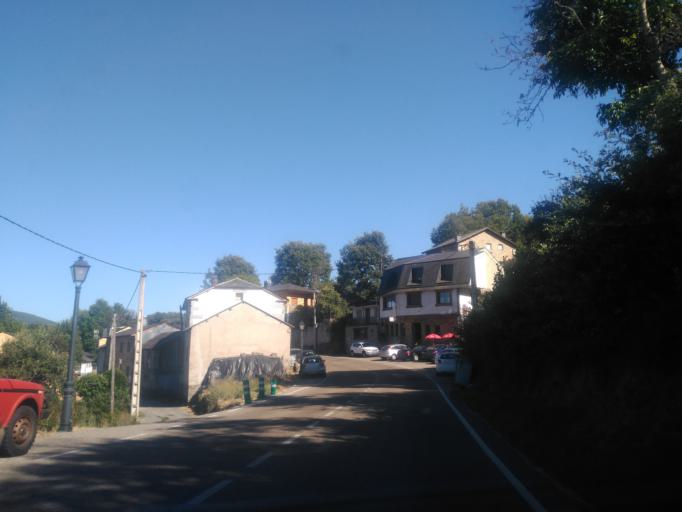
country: ES
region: Castille and Leon
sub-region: Provincia de Zamora
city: Galende
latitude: 42.1050
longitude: -6.6648
